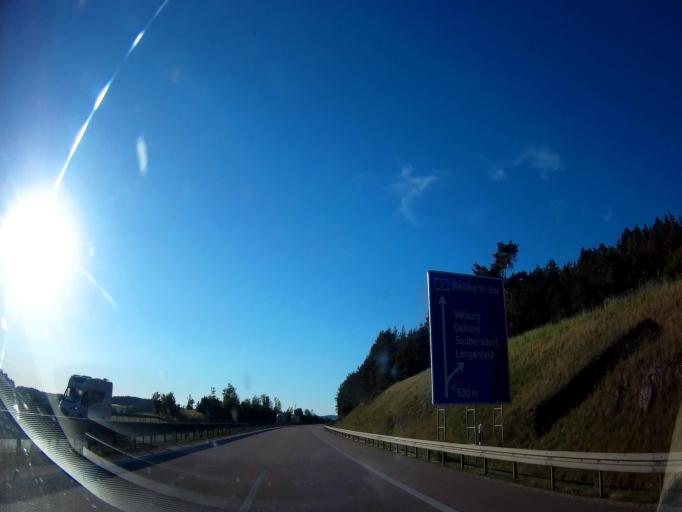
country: DE
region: Bavaria
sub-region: Upper Palatinate
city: Velburg
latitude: 49.2273
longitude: 11.6413
